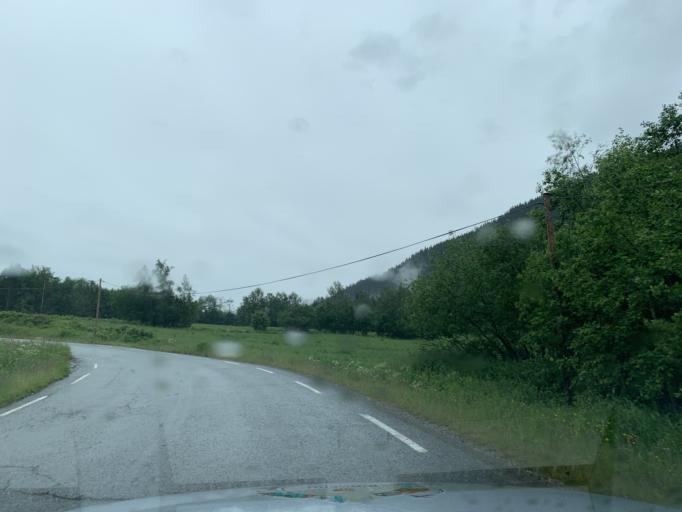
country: NO
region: Oppland
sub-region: Ringebu
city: Ringebu
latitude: 61.4480
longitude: 10.1696
